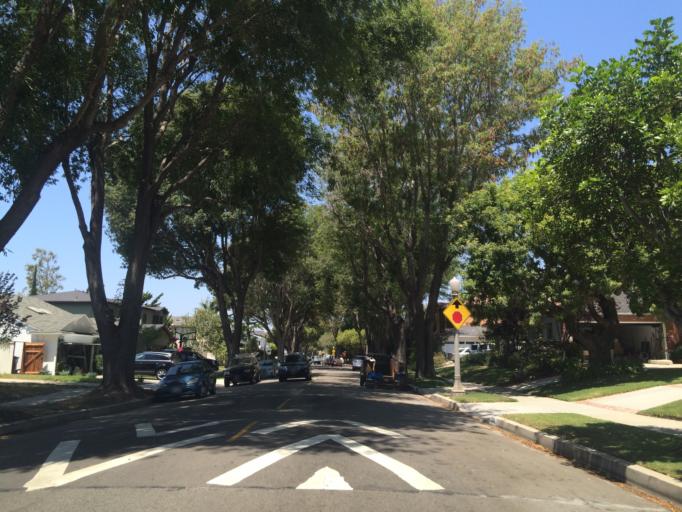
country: US
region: California
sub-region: Los Angeles County
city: Culver City
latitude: 34.0425
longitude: -118.3975
